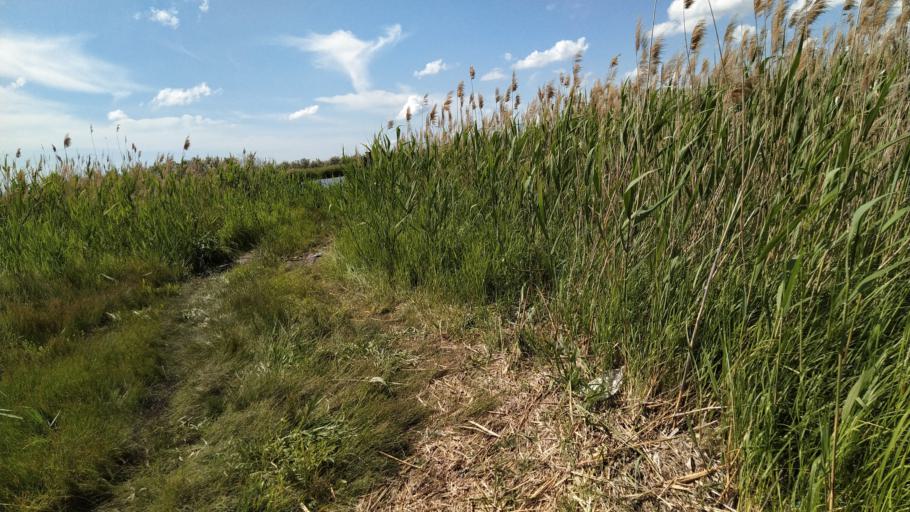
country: RU
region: Rostov
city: Bataysk
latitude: 47.1357
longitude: 39.6710
